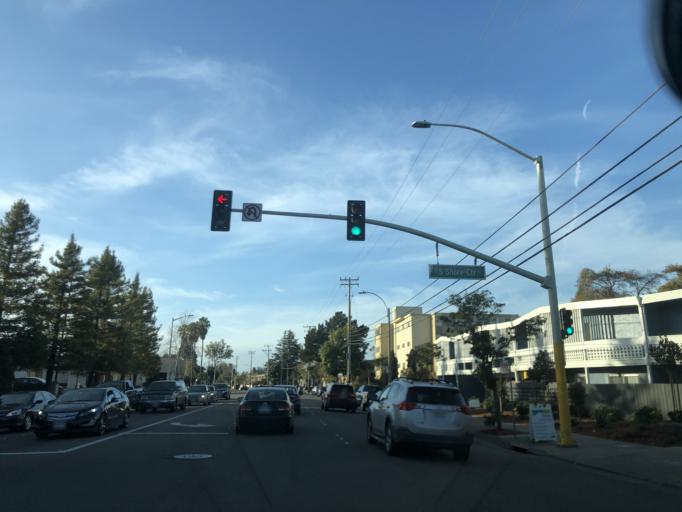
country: US
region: California
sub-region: Alameda County
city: Alameda
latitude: 37.7597
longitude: -122.2520
